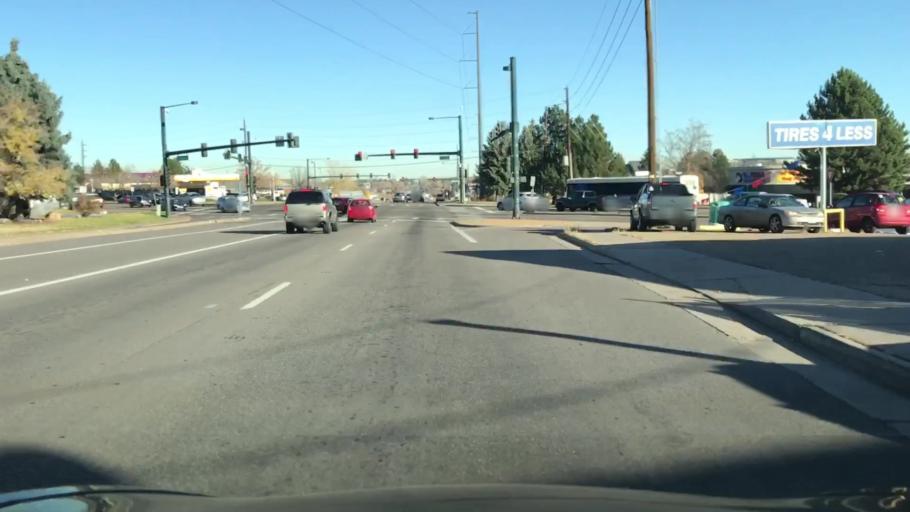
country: US
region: Colorado
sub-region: Arapahoe County
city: Glendale
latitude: 39.6759
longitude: -104.9035
